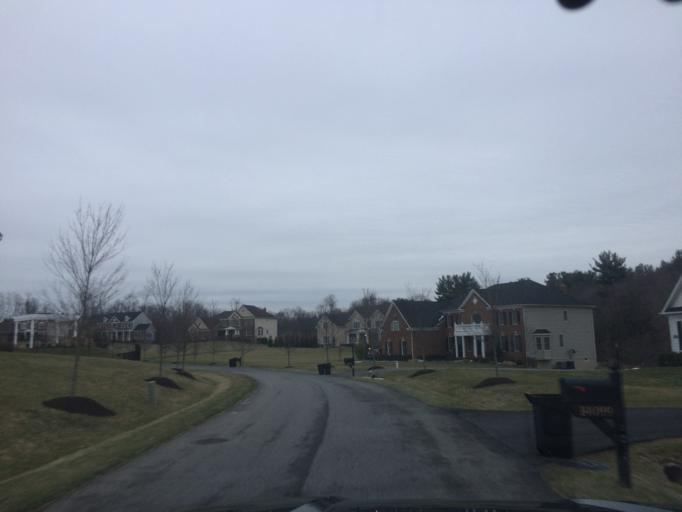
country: US
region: Maryland
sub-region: Howard County
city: Highland
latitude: 39.2667
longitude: -77.0031
